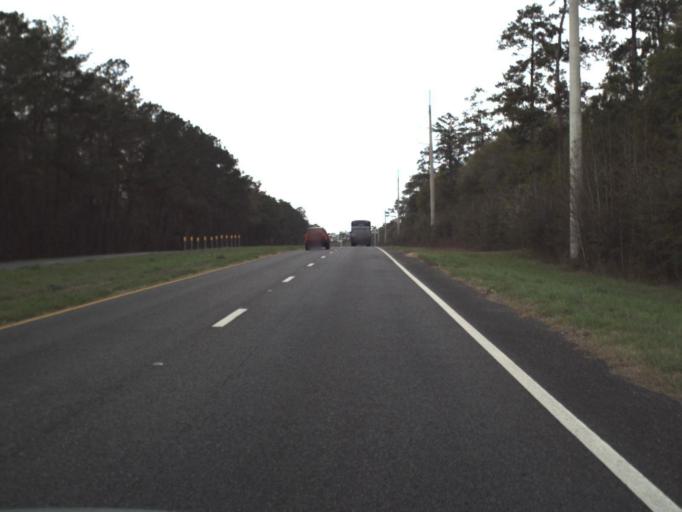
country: US
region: Florida
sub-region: Leon County
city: Woodville
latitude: 30.4091
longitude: -84.0662
